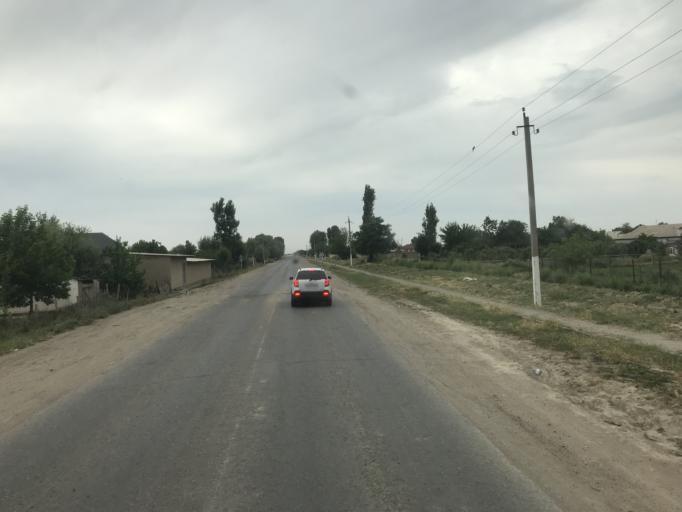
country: KZ
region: Ongtustik Qazaqstan
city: Asykata
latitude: 40.9041
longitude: 68.3557
